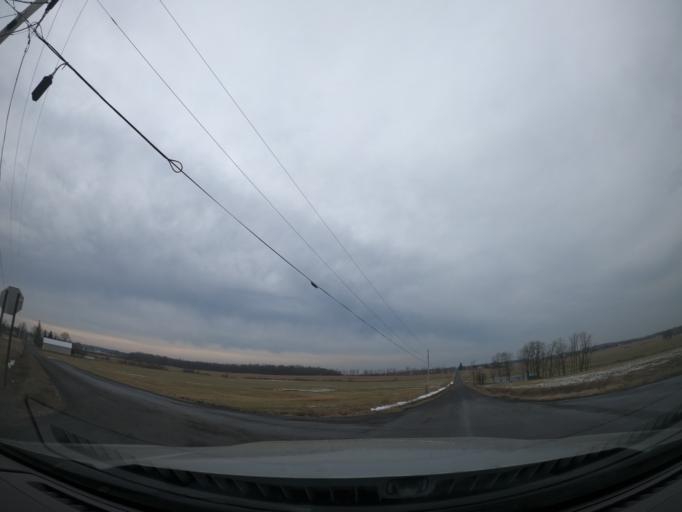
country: US
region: New York
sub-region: Cayuga County
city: Melrose Park
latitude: 42.8392
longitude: -76.5580
